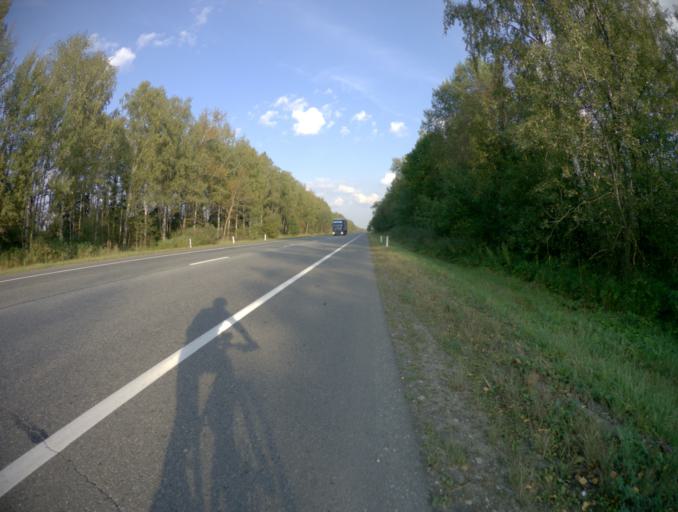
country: RU
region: Vladimir
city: Kameshkovo
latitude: 56.1975
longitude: 40.8569
